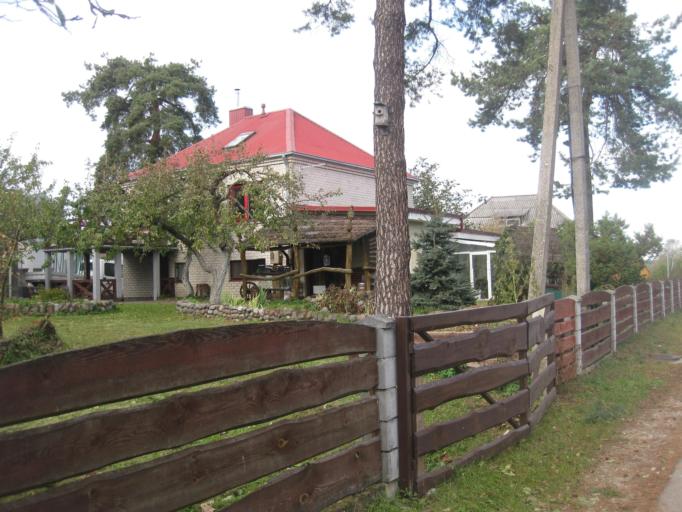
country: LT
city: Ezerelis
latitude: 54.8815
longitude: 23.6142
